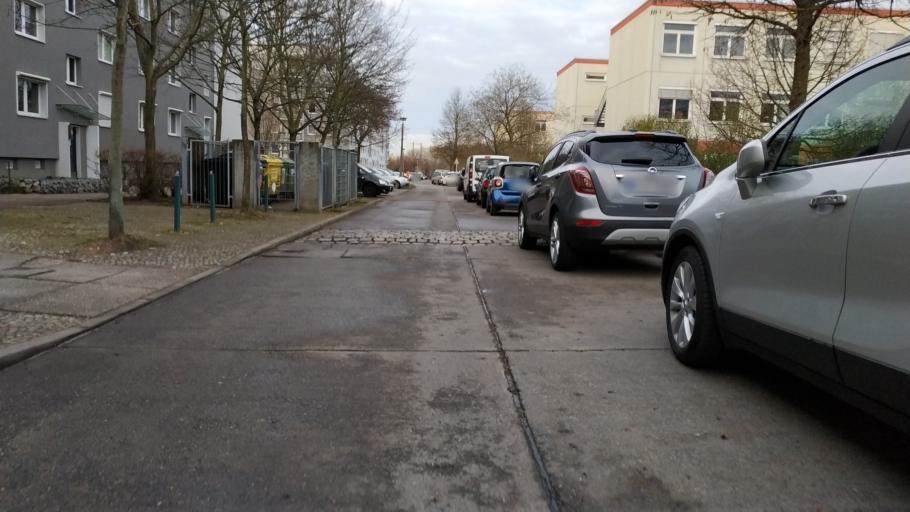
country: DE
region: Berlin
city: Marzahn
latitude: 52.5424
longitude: 13.5878
